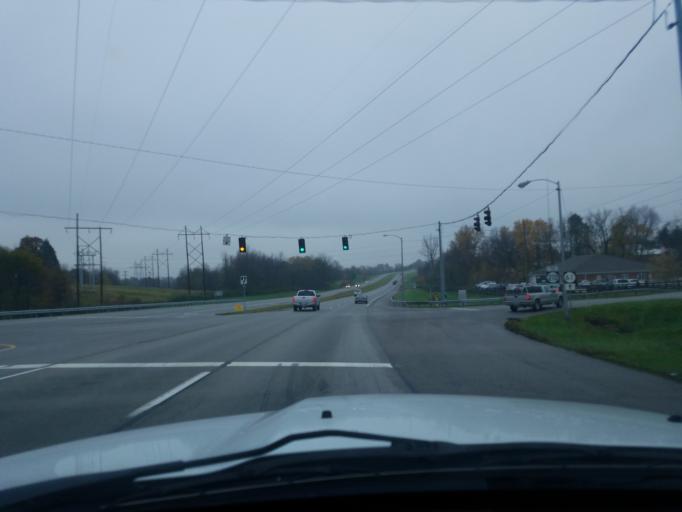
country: US
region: Kentucky
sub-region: Hardin County
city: Elizabethtown
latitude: 37.6658
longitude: -85.8400
